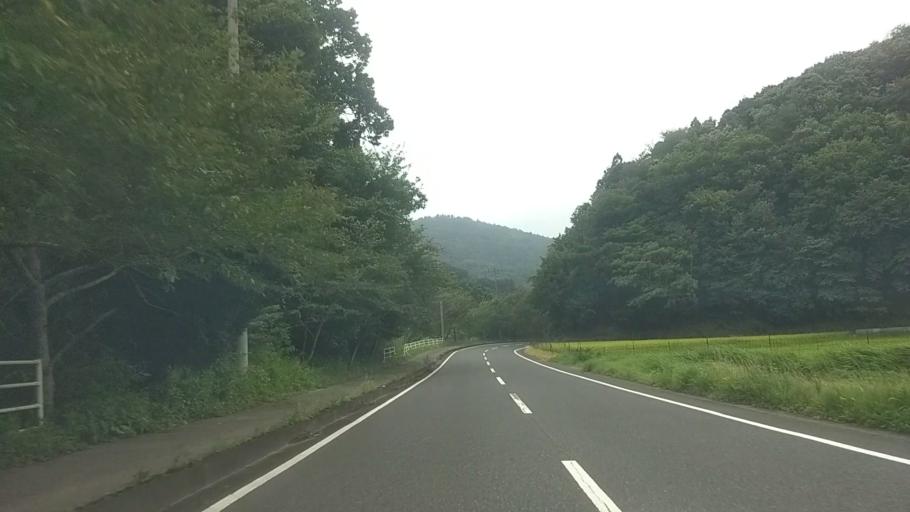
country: JP
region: Chiba
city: Kawaguchi
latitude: 35.2500
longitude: 140.0391
